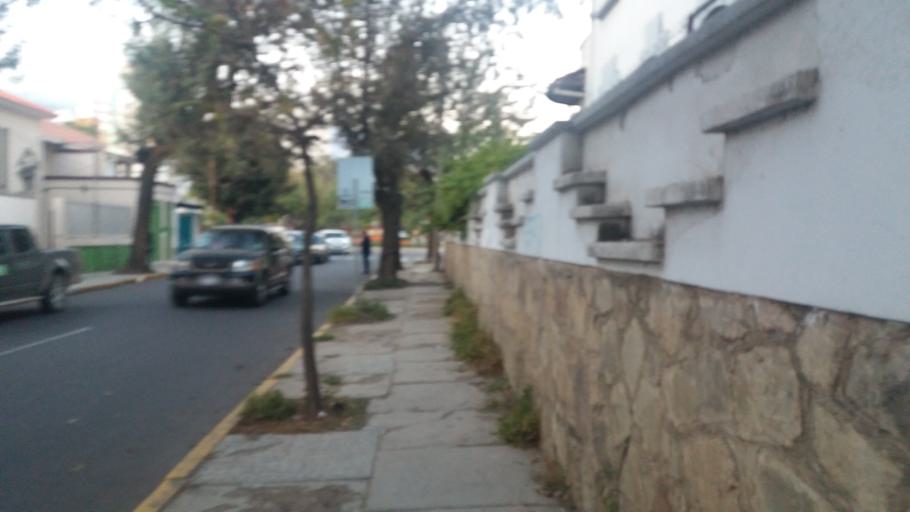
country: BO
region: Cochabamba
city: Cochabamba
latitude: -17.3849
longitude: -66.1540
